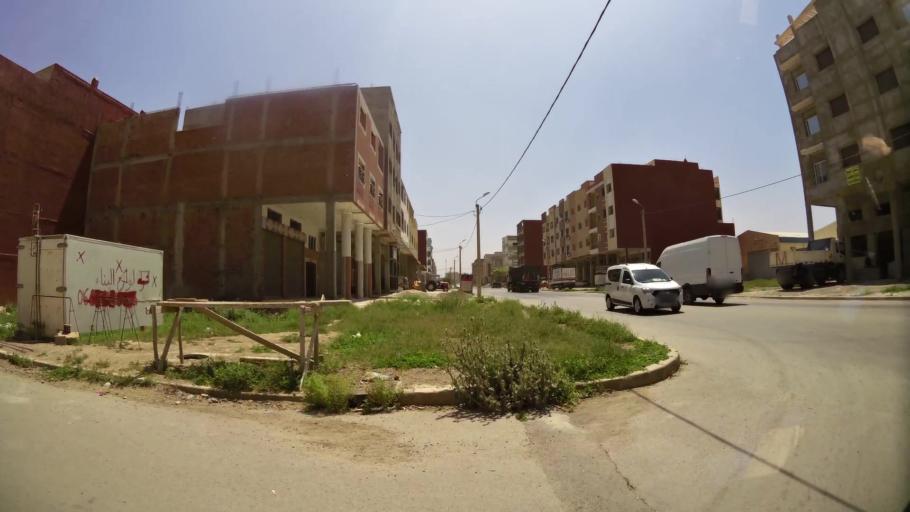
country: MA
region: Oriental
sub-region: Oujda-Angad
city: Oujda
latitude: 34.7021
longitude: -1.8894
